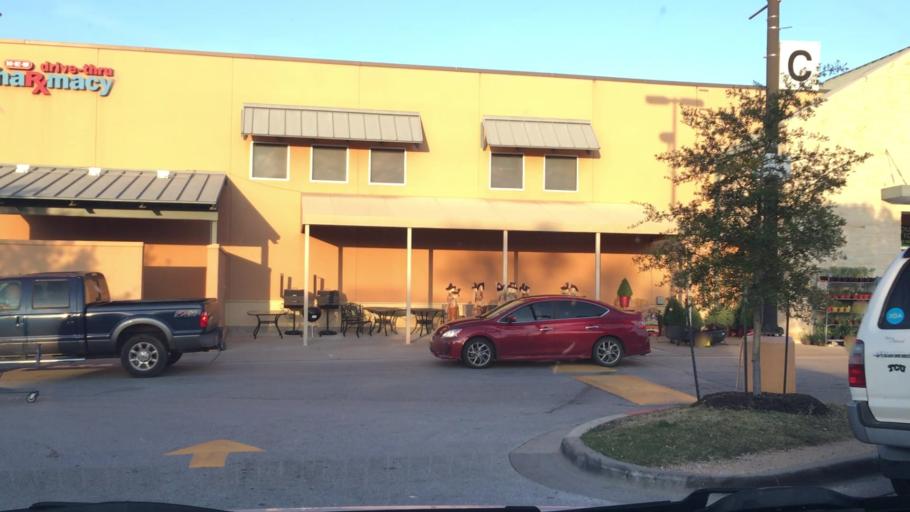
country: US
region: Texas
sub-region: Travis County
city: Bee Cave
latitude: 30.3046
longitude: -97.9331
